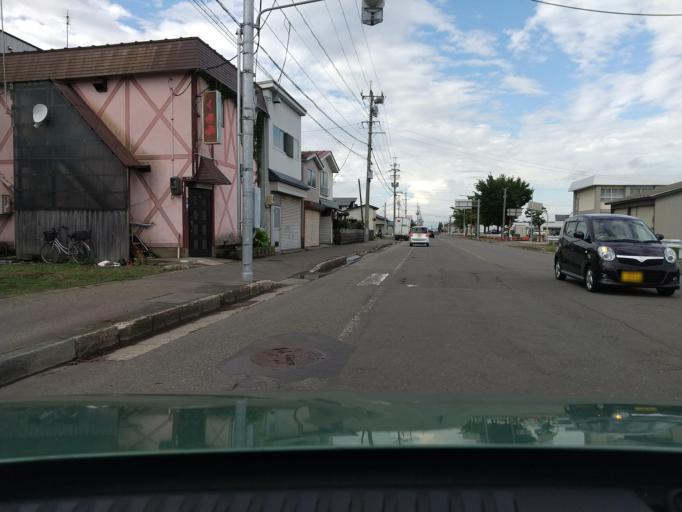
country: JP
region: Akita
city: Yokotemachi
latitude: 39.2619
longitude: 140.4906
